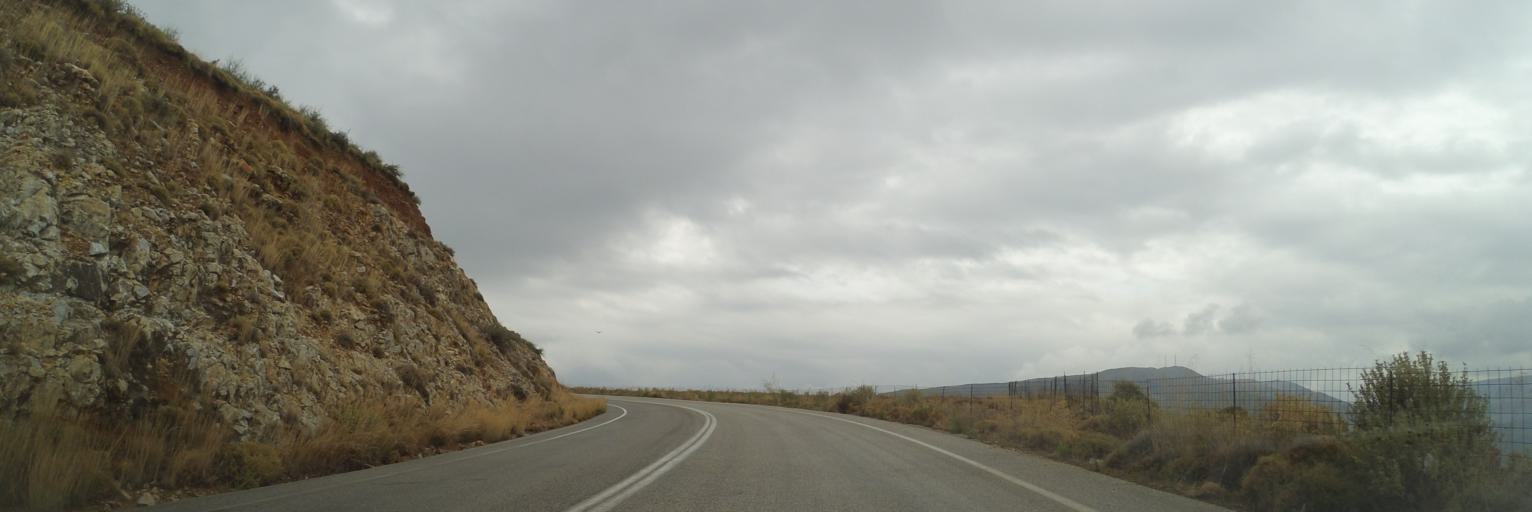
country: GR
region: Crete
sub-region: Nomos Rethymnis
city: Agia Foteini
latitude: 35.2940
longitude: 24.5647
